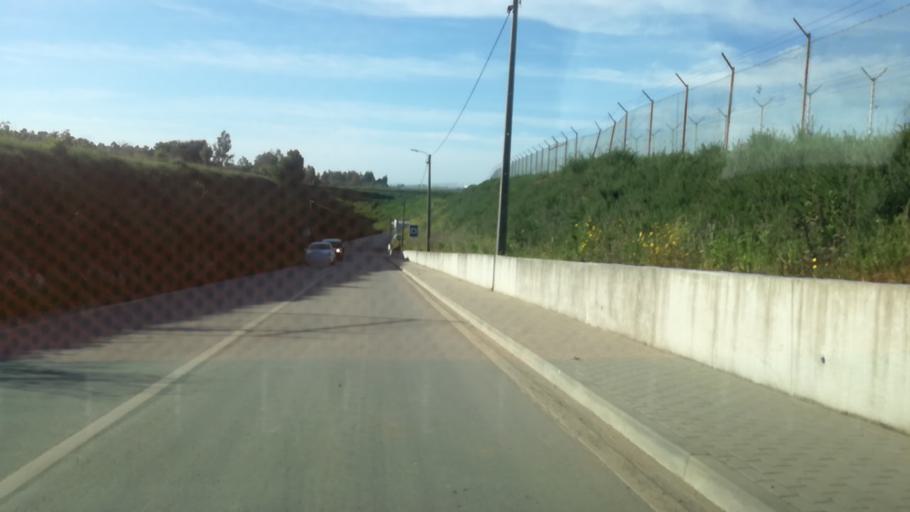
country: PT
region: Porto
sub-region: Matosinhos
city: Santa Cruz do Bispo
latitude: 41.2490
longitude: -8.6843
